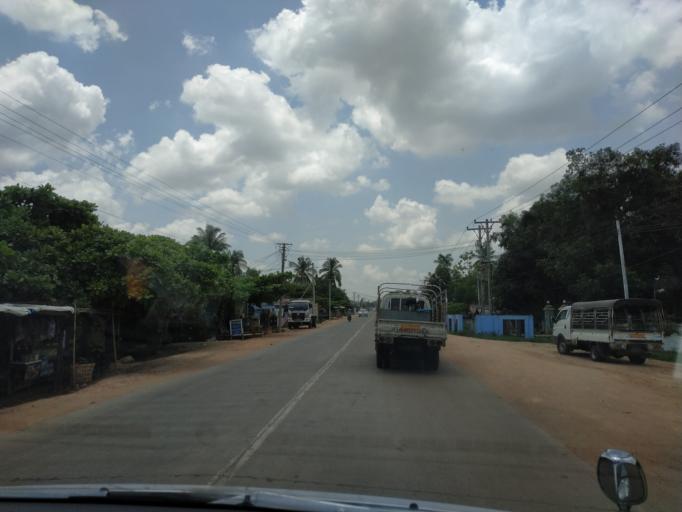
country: MM
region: Bago
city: Bago
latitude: 17.4759
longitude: 96.5223
